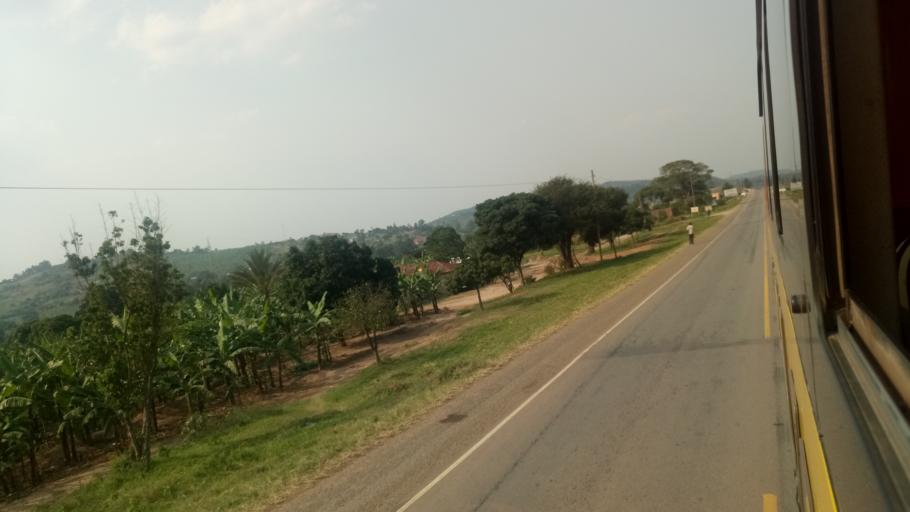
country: UG
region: Western Region
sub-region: Mbarara District
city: Mbarara
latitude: -0.5273
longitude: 30.7264
